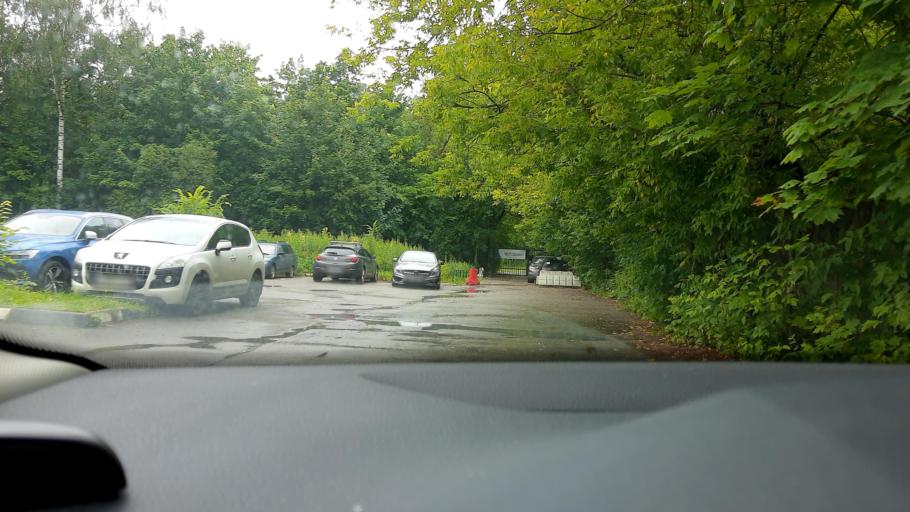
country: RU
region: Moscow
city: Khimki
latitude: 55.8656
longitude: 37.4277
